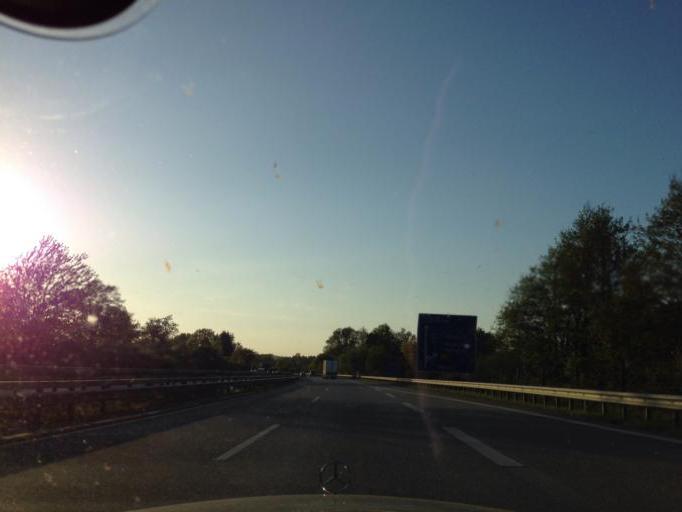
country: DE
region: Schleswig-Holstein
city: Schackendorf
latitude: 53.9622
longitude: 10.2595
